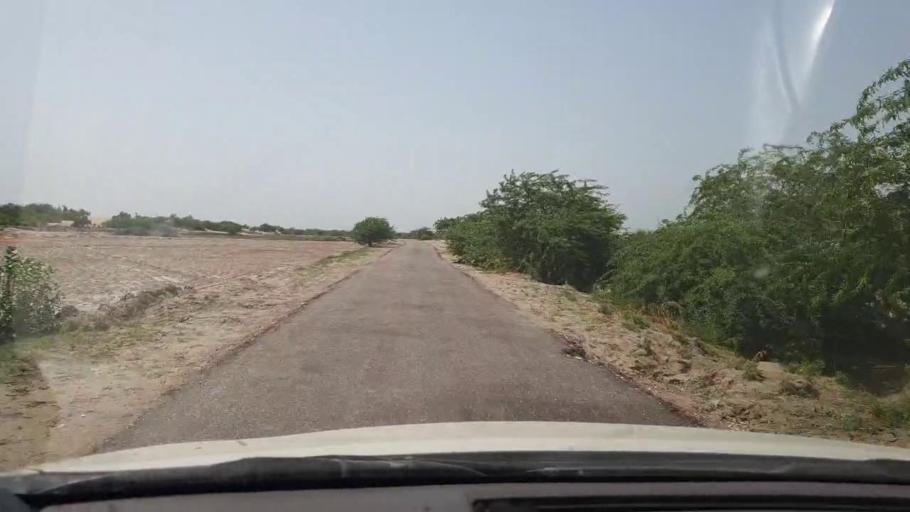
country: PK
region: Sindh
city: Rohri
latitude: 27.5196
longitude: 69.0743
